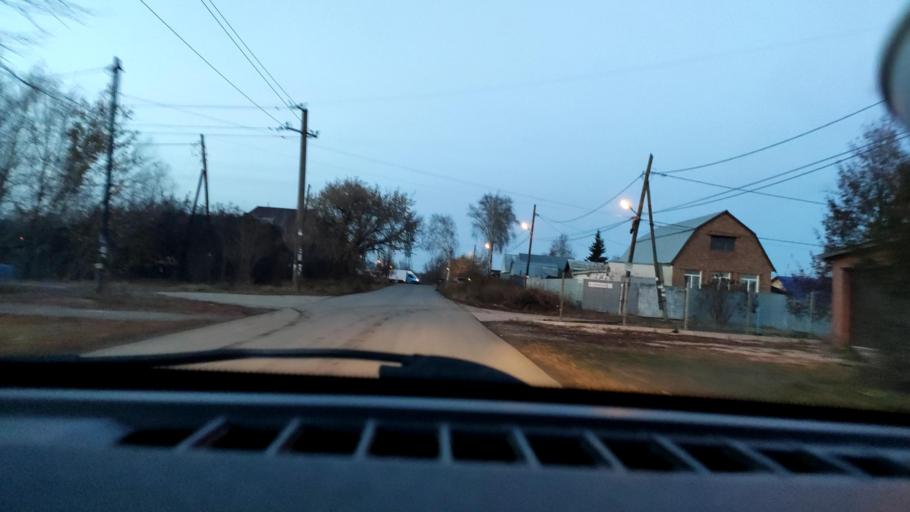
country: RU
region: Samara
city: Petra-Dubrava
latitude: 53.2612
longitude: 50.3298
